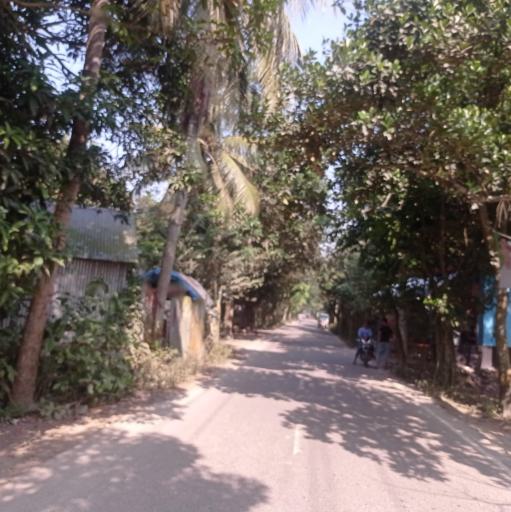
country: BD
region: Dhaka
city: Narsingdi
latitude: 24.0382
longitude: 90.6768
